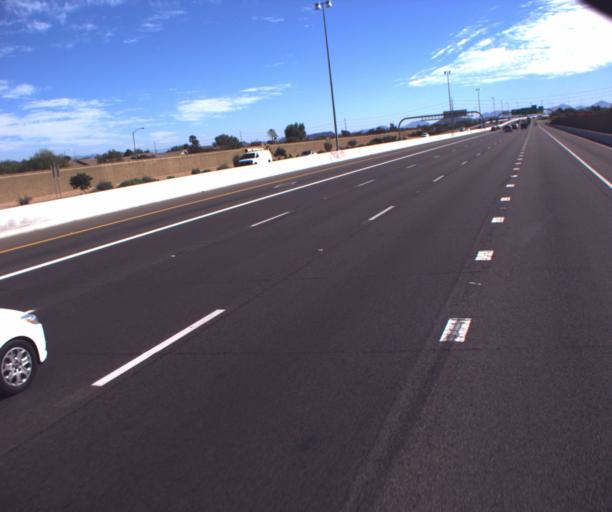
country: US
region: Arizona
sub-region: Maricopa County
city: Peoria
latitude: 33.6694
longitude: -112.1439
